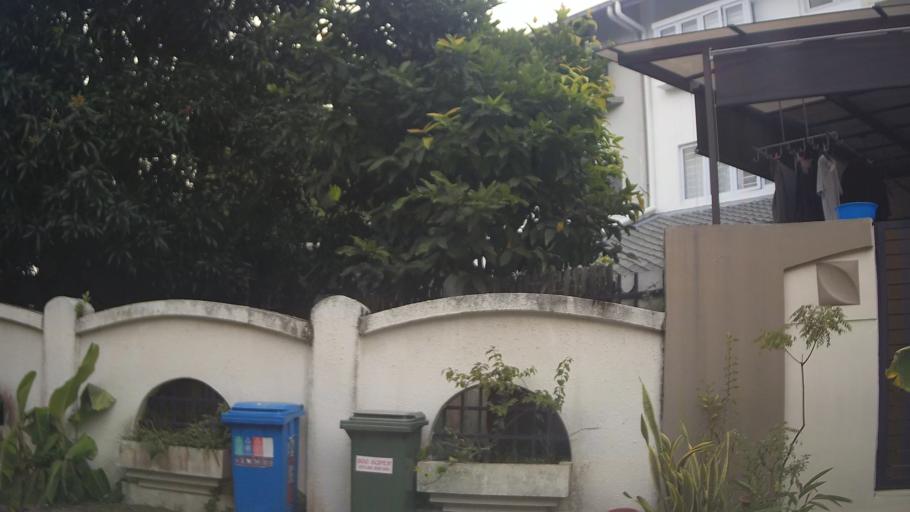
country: MY
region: Johor
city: Kampung Pasir Gudang Baru
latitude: 1.3860
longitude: 103.8573
